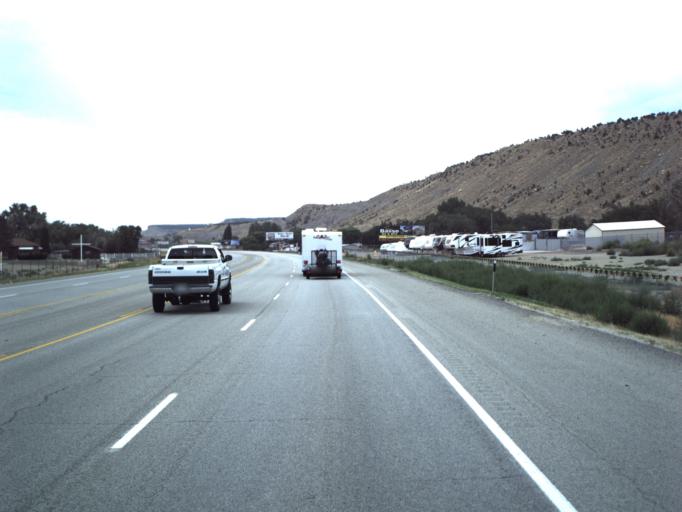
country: US
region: Utah
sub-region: Carbon County
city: Helper
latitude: 39.6777
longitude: -110.8612
